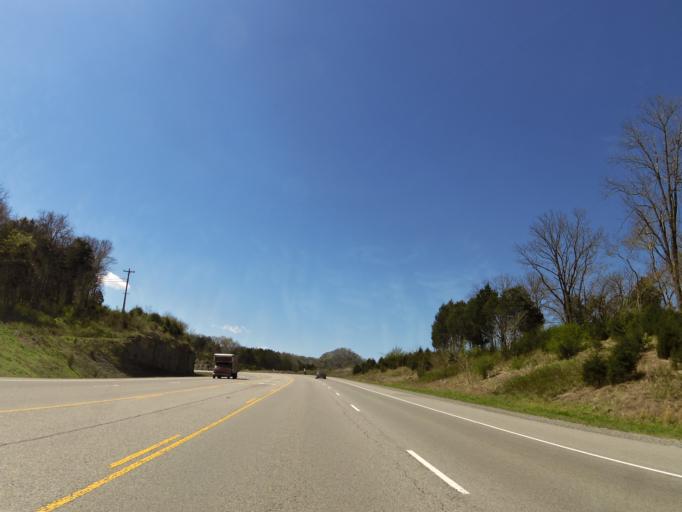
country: US
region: Tennessee
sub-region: DeKalb County
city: Smithville
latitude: 36.0147
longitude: -85.9528
